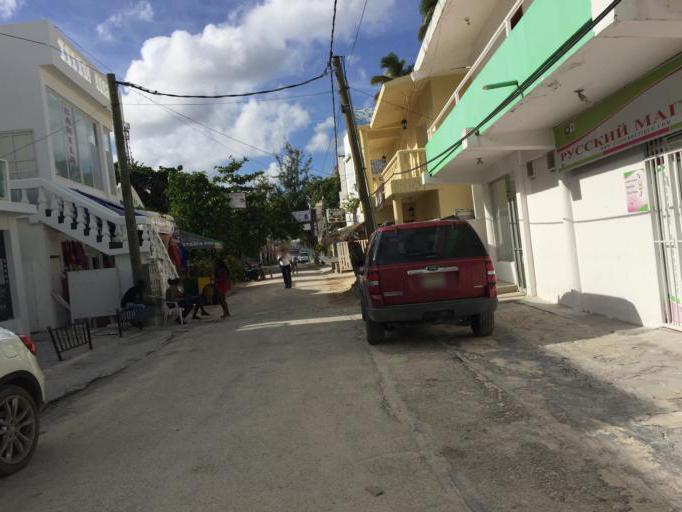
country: DO
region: San Juan
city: Punta Cana
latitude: 18.6919
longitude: -68.4221
